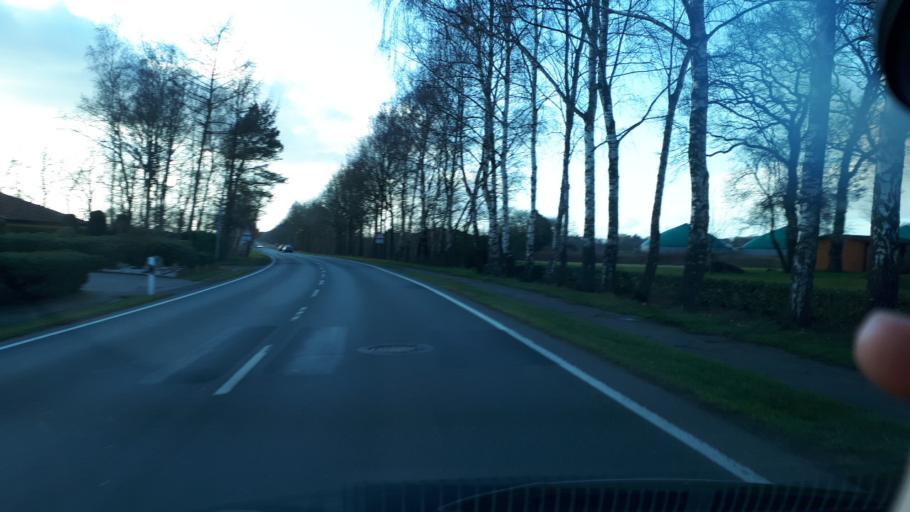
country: DE
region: Lower Saxony
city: Molbergen
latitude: 52.8652
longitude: 7.9102
